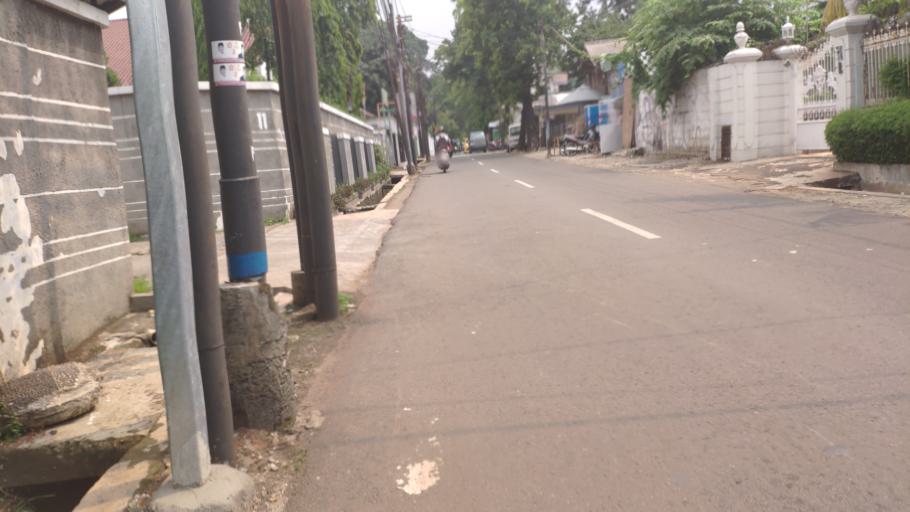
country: ID
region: Jakarta Raya
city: Jakarta
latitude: -6.2599
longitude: 106.8233
